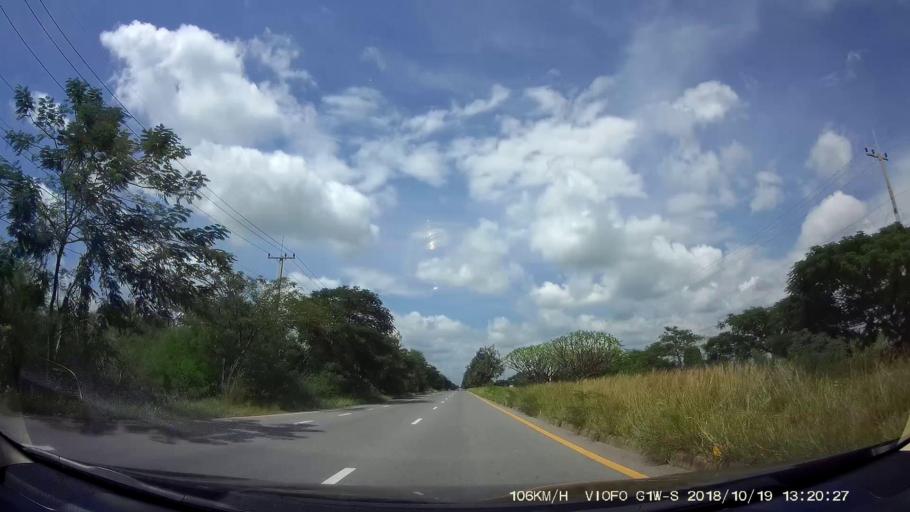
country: TH
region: Chaiyaphum
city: Chatturat
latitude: 15.4461
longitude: 101.8285
